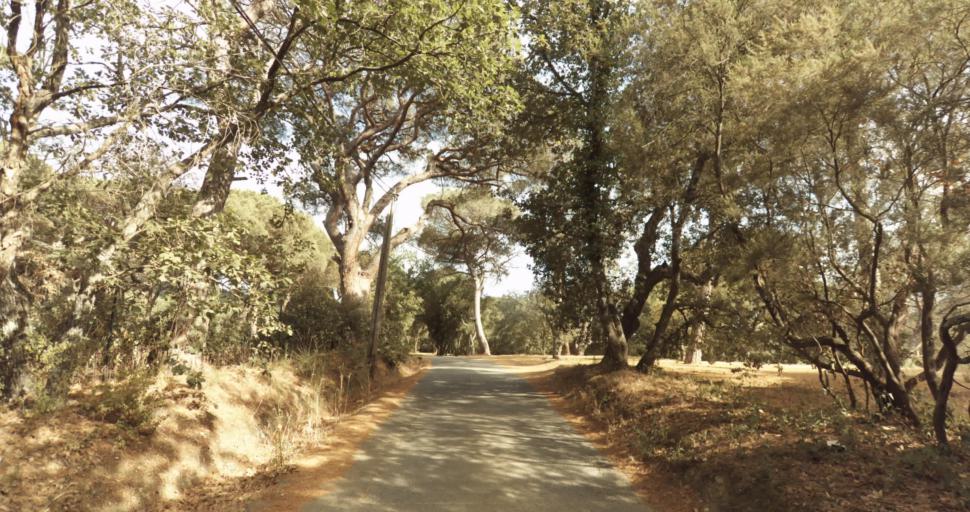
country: FR
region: Provence-Alpes-Cote d'Azur
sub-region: Departement du Var
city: Gassin
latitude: 43.2246
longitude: 6.5782
